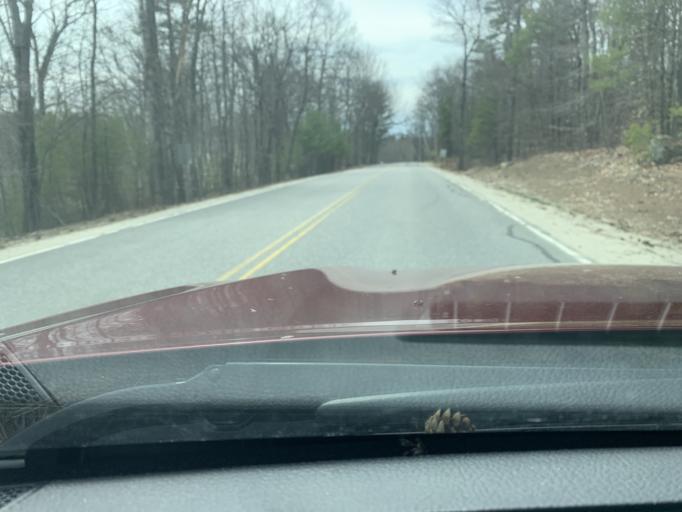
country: US
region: Maine
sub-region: Cumberland County
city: Raymond
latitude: 43.9450
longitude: -70.3855
